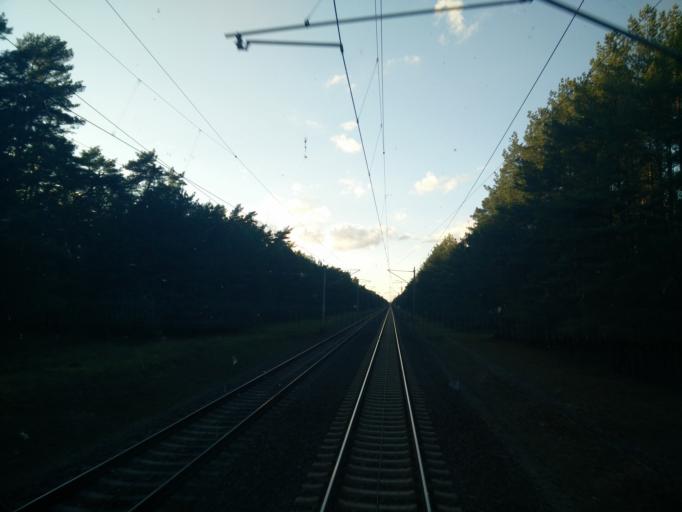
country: DE
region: Brandenburg
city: Plattenburg
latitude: 52.9370
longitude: 12.0034
